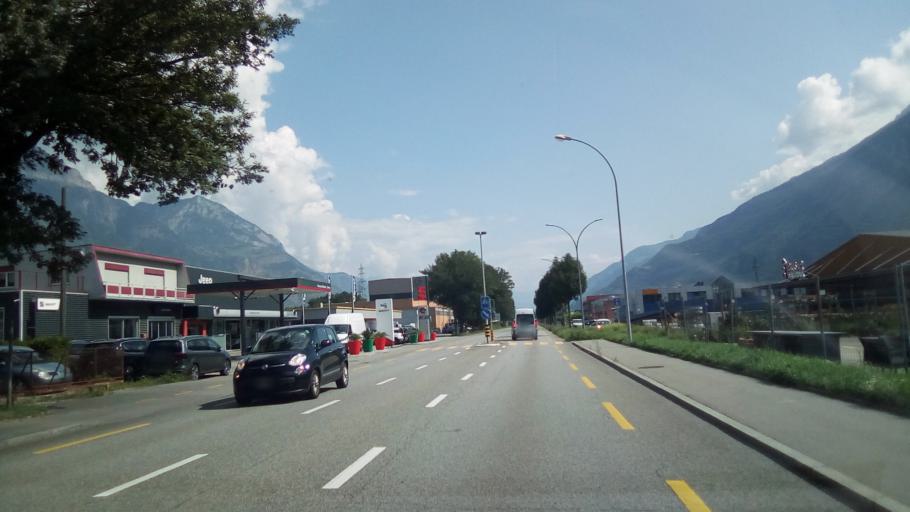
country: CH
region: Valais
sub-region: Martigny District
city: Martigny-Ville
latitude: 46.1091
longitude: 7.0912
